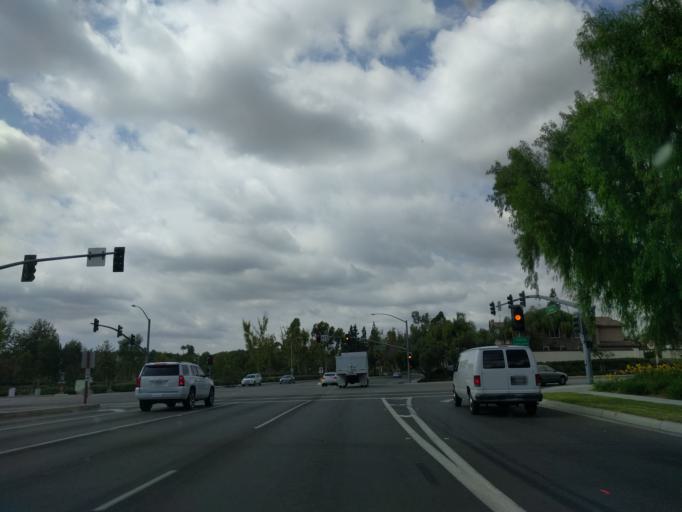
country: US
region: California
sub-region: Orange County
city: North Tustin
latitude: 33.7437
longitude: -117.7708
